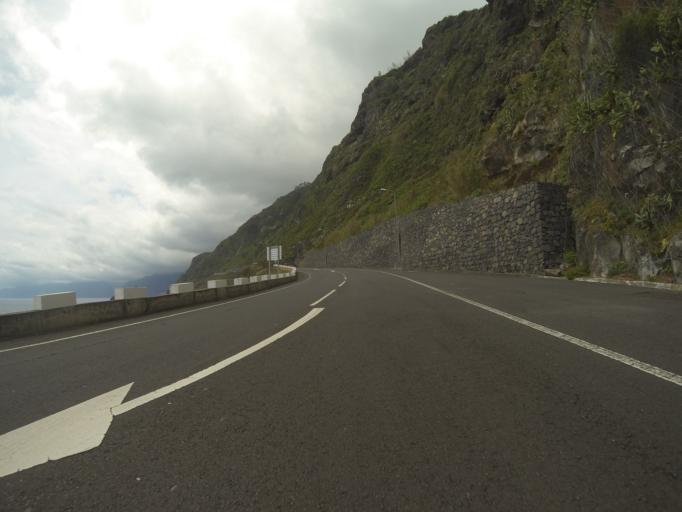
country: PT
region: Madeira
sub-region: Porto Moniz
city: Porto Moniz
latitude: 32.8606
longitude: -17.1644
